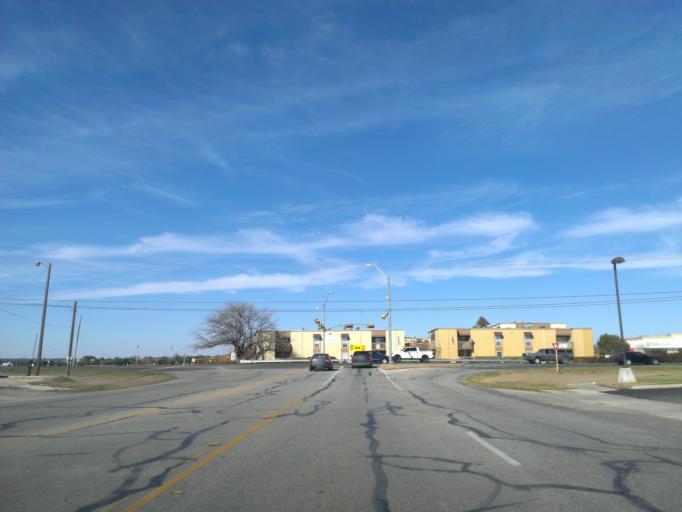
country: US
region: Texas
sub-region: Bell County
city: Harker Heights
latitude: 31.1153
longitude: -97.6844
